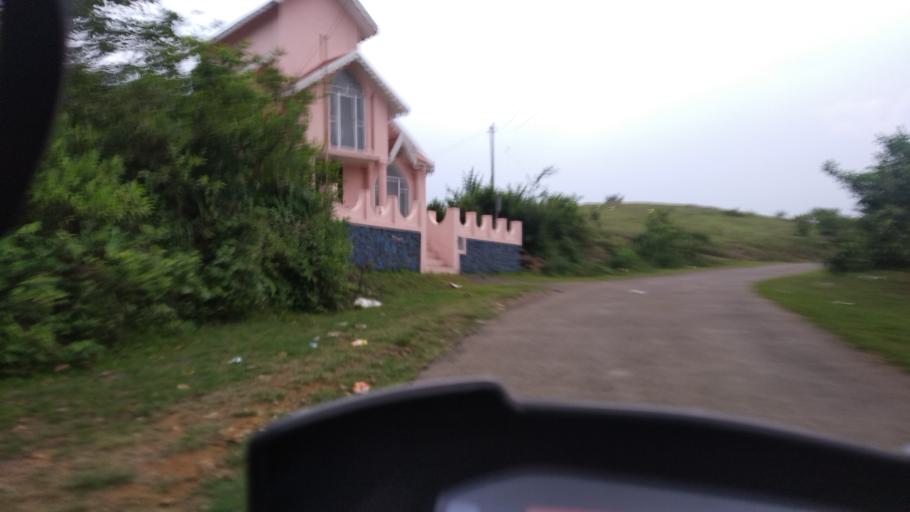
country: IN
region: Tamil Nadu
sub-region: Theni
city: Gudalur
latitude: 9.5484
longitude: 77.0339
